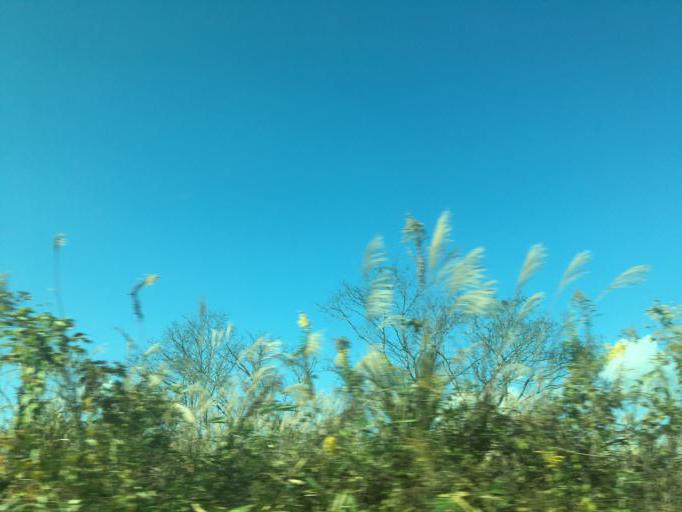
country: JP
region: Ibaraki
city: Kasama
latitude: 36.3759
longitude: 140.2284
